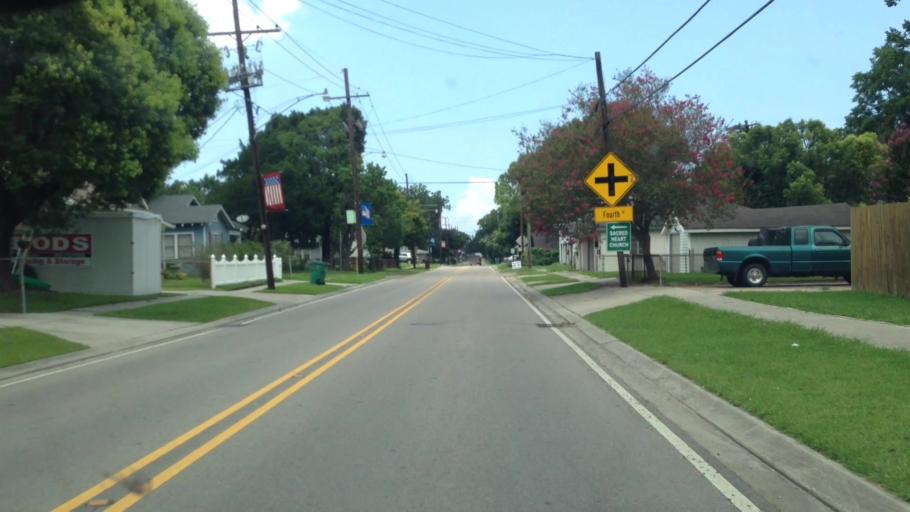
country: US
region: Louisiana
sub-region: Saint Charles Parish
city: Norco
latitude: 30.0041
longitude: -90.4110
